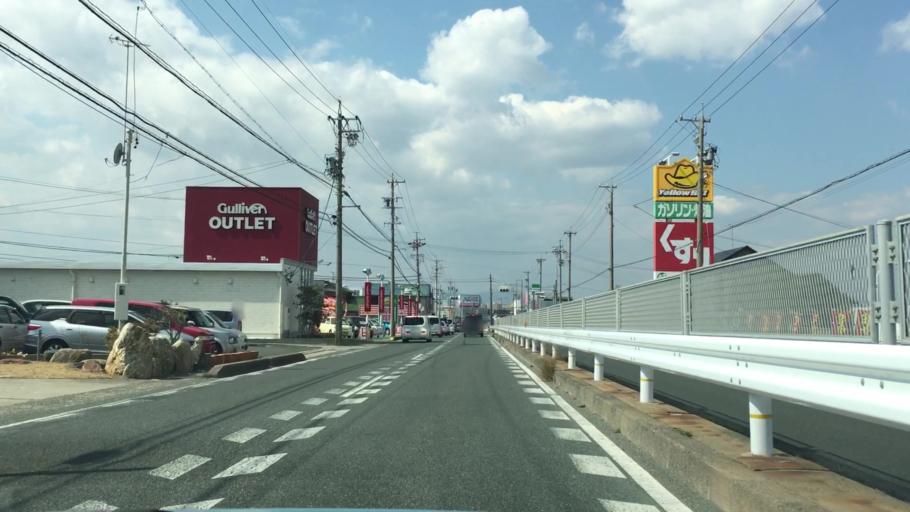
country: JP
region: Aichi
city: Toyohashi
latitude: 34.7418
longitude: 137.4185
